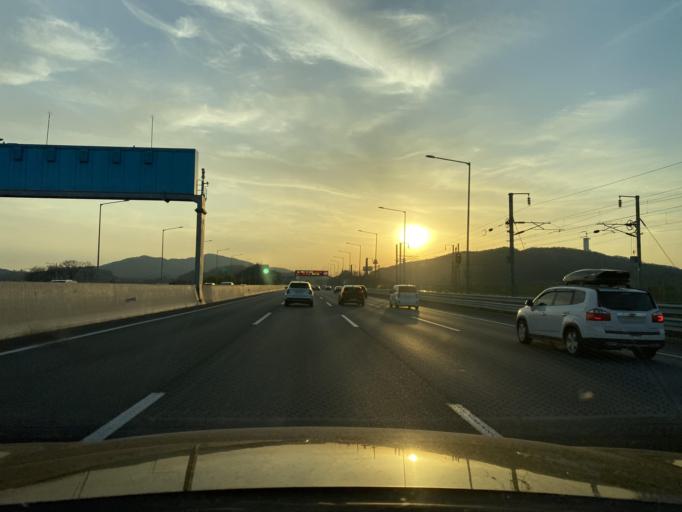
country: KR
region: Incheon
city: Incheon
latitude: 37.5226
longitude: 126.5433
